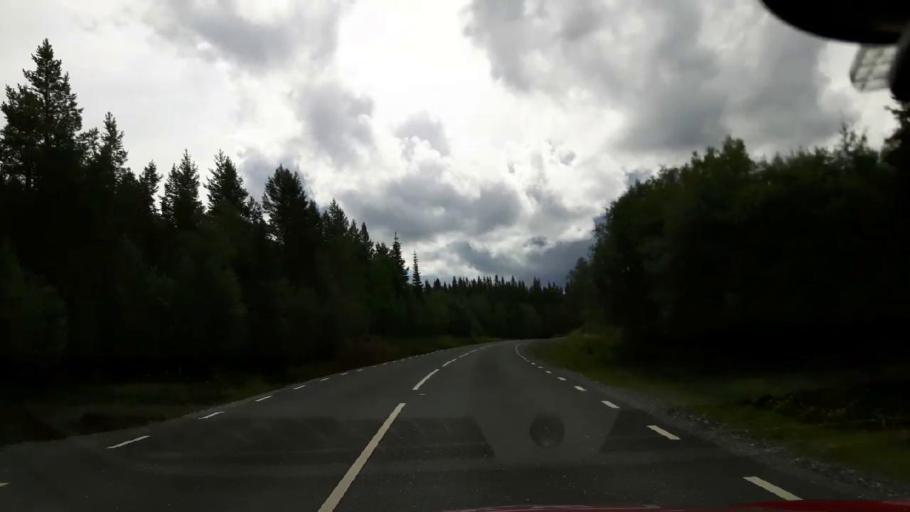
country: NO
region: Nord-Trondelag
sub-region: Lierne
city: Sandvika
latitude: 64.5992
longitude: 14.1206
